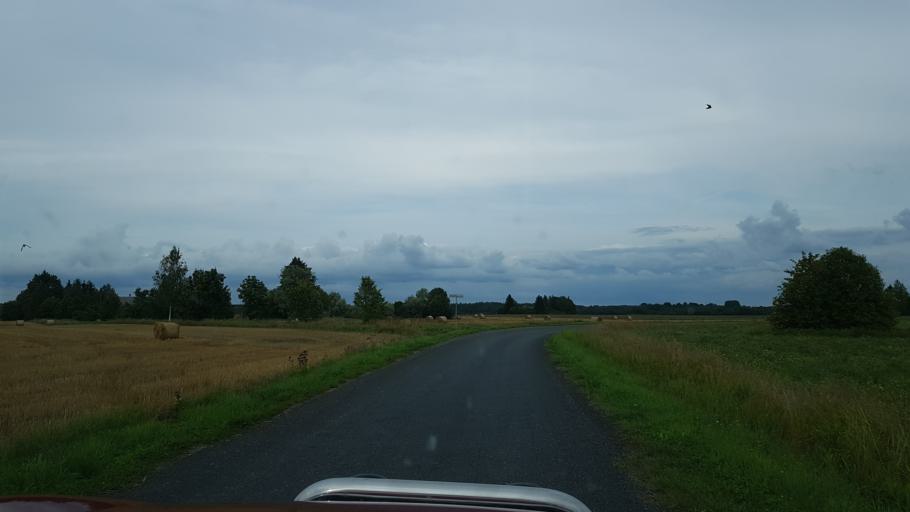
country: EE
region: Laeaene
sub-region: Ridala Parish
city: Uuemoisa
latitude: 58.9822
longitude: 23.7926
